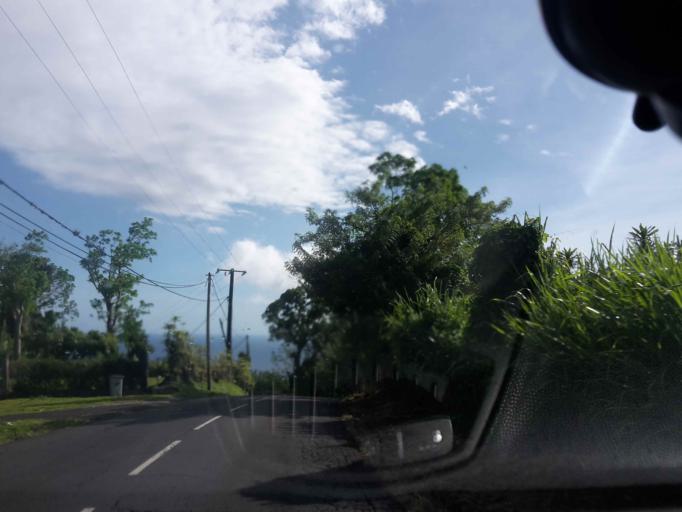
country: GP
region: Guadeloupe
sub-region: Guadeloupe
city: Gourbeyre
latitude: 16.0084
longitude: -61.6961
